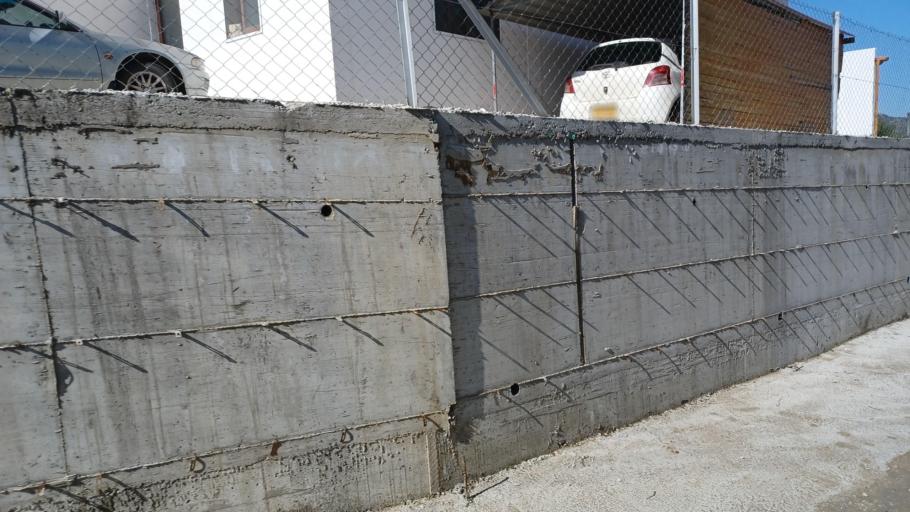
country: CY
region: Limassol
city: Kyperounta
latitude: 35.0256
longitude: 33.0403
